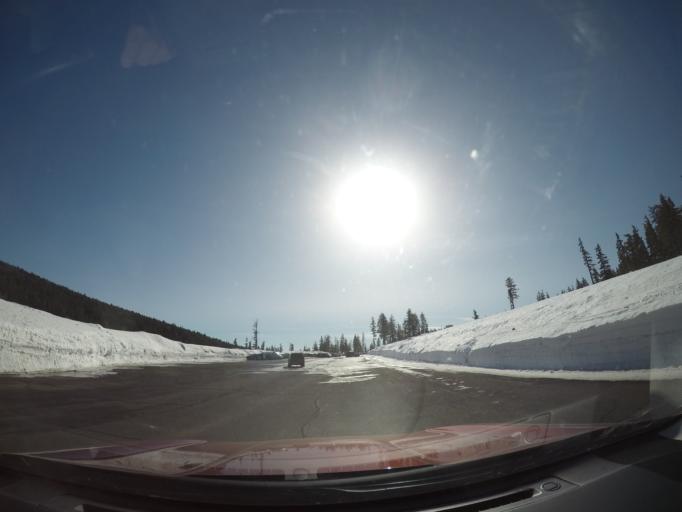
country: US
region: Oregon
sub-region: Deschutes County
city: Sunriver
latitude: 43.9941
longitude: -121.6629
